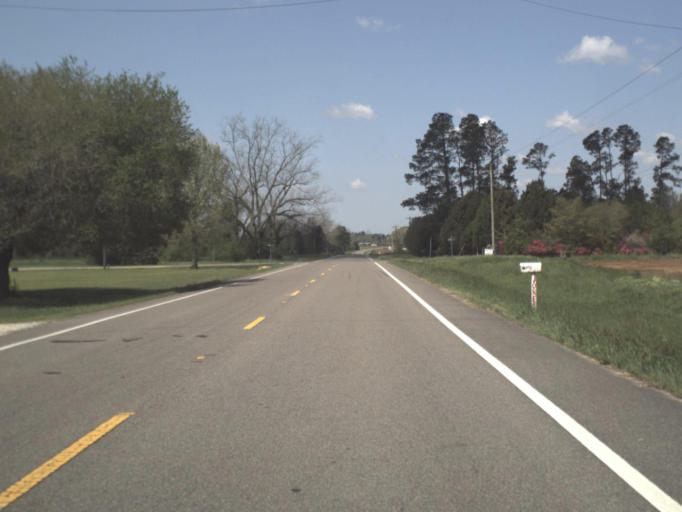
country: US
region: Alabama
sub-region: Escambia County
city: East Brewton
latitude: 30.8996
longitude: -87.0127
